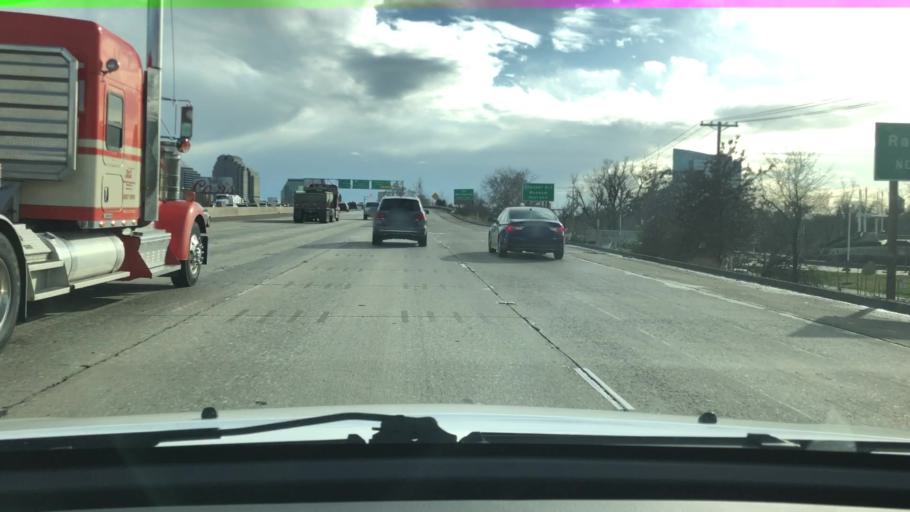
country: US
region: California
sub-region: Sacramento County
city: Sacramento
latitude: 38.5928
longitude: -121.5046
